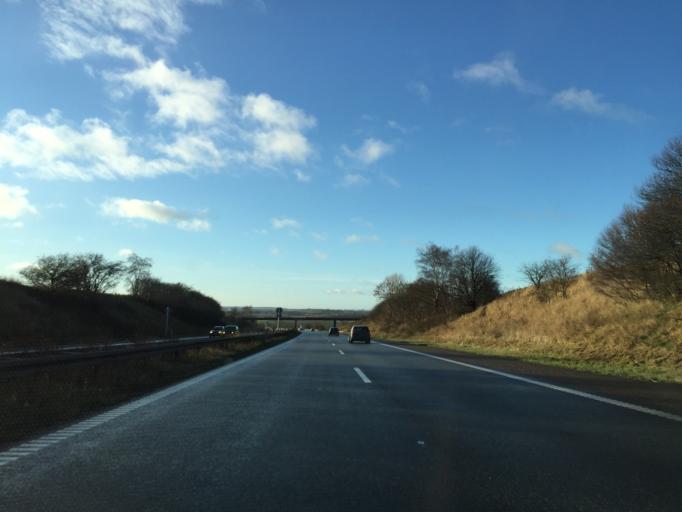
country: DK
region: Zealand
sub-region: Slagelse Kommune
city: Forlev
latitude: 55.3773
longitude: 11.3122
